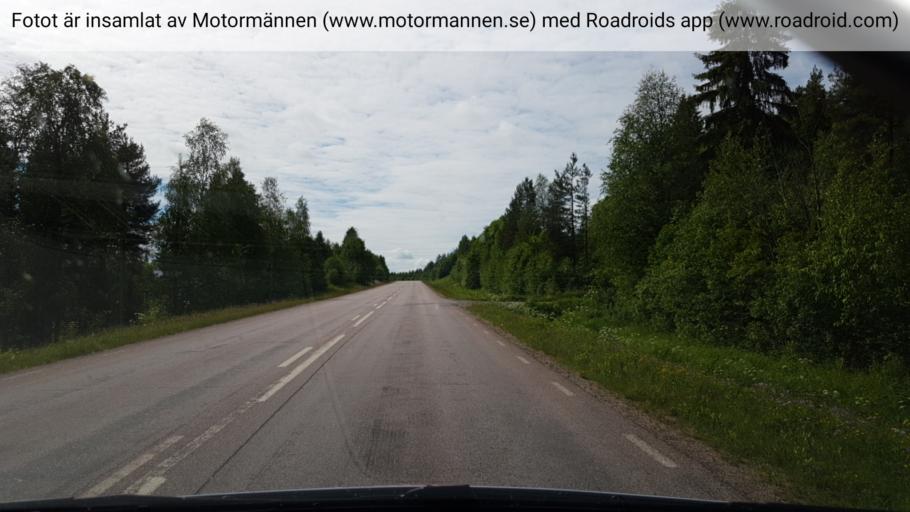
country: SE
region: Norrbotten
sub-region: Overtornea Kommun
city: OEvertornea
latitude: 66.4542
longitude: 23.6240
